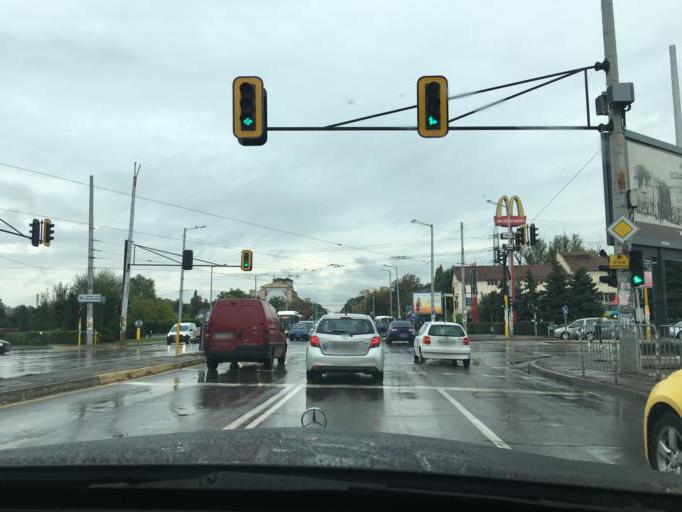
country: BG
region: Sofia-Capital
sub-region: Stolichna Obshtina
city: Sofia
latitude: 42.7178
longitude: 23.2784
